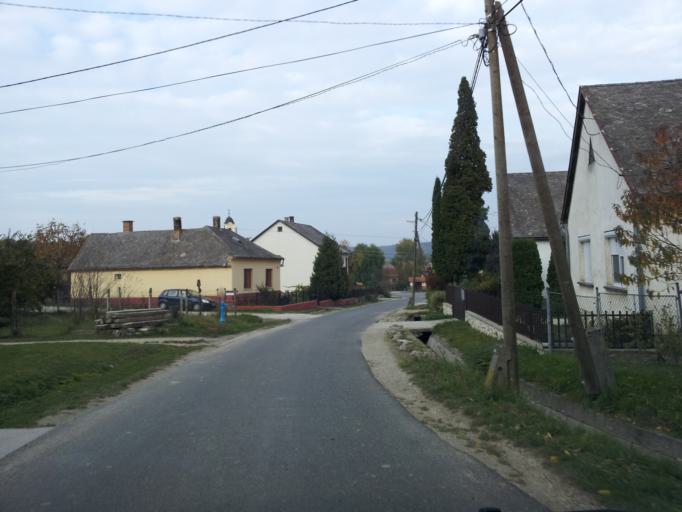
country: HU
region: Gyor-Moson-Sopron
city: Pannonhalma
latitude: 47.5094
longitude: 17.7504
